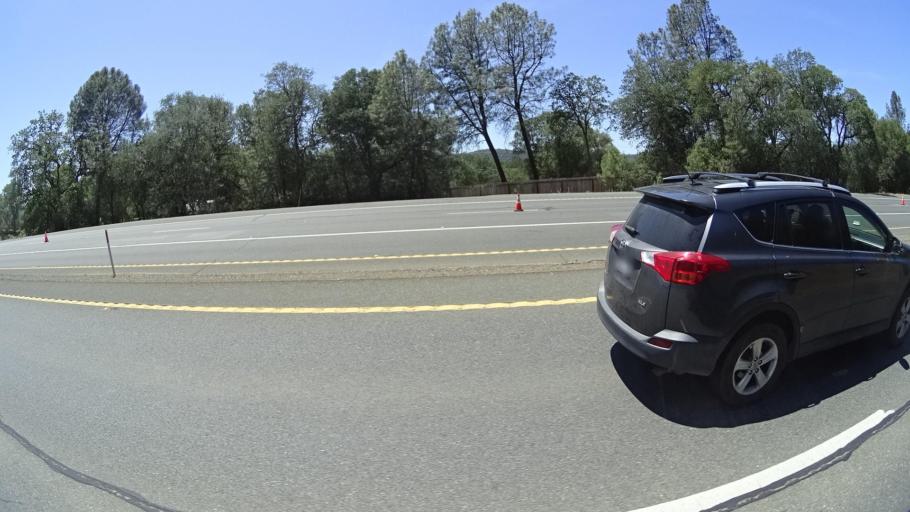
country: US
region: California
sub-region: Lake County
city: Clearlake
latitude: 38.9384
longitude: -122.6230
